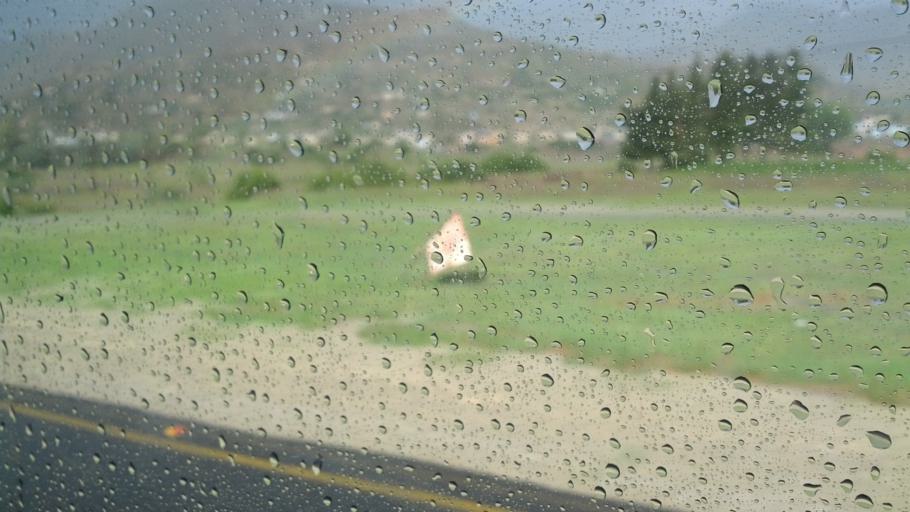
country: LS
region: Mafeteng
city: Mafeteng
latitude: -29.8456
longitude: 27.2293
